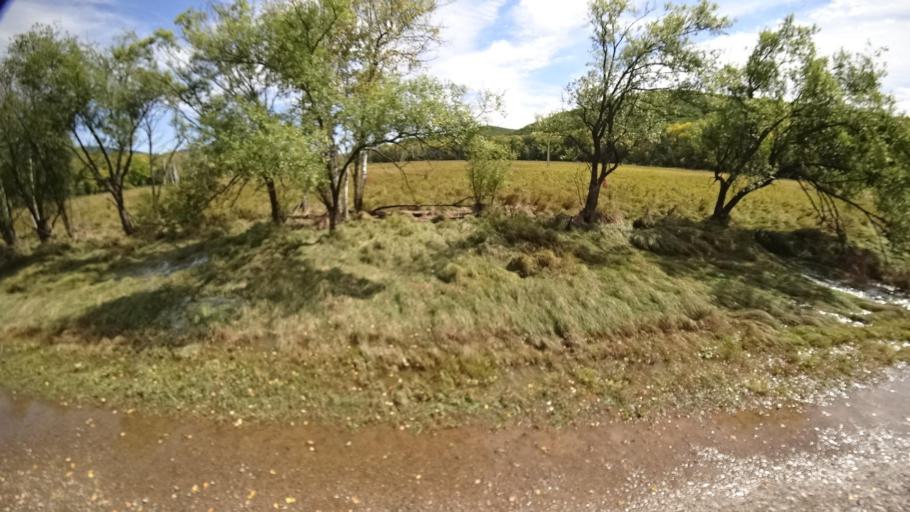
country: RU
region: Primorskiy
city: Yakovlevka
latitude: 44.6617
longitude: 133.7499
